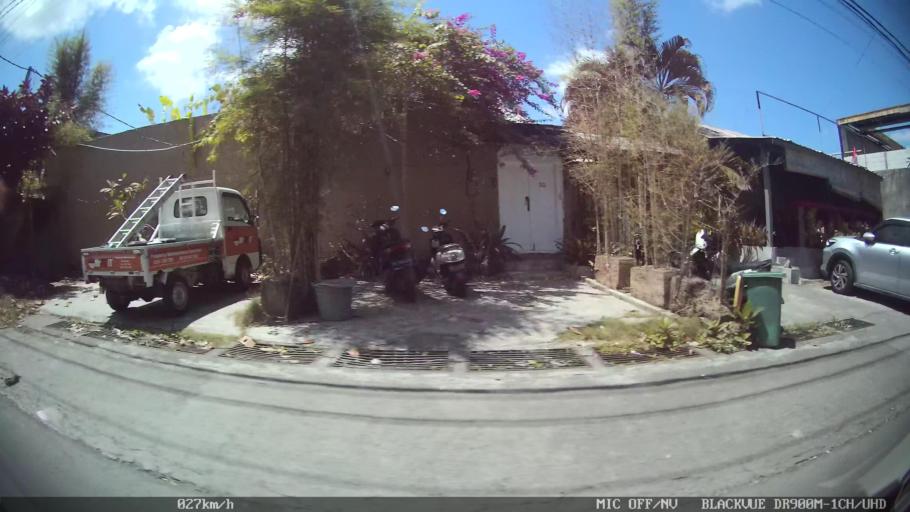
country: ID
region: Bali
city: Banjar Gunungpande
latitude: -8.6625
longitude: 115.1524
